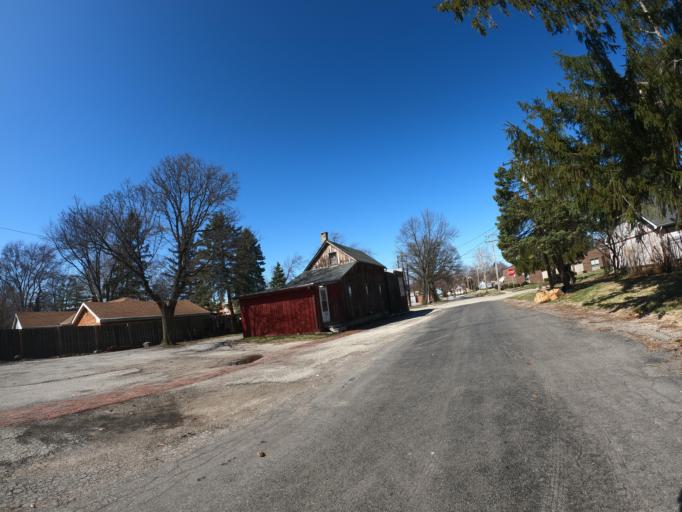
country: US
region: Illinois
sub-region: Sangamon County
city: Springfield
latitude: 39.8071
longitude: -89.6614
